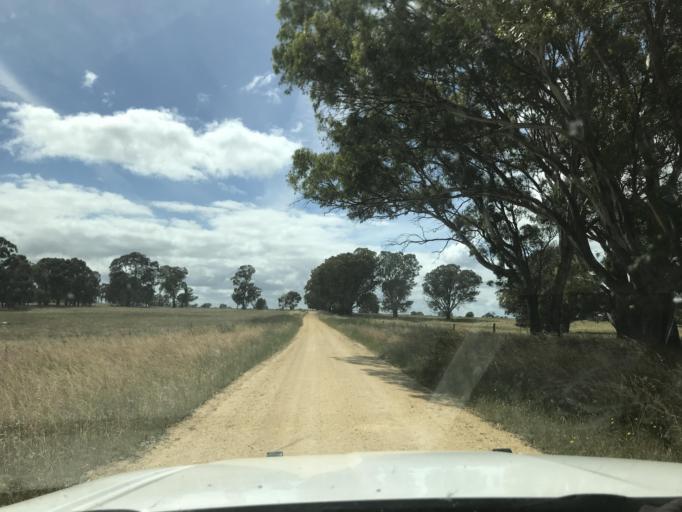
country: AU
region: South Australia
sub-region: Naracoorte and Lucindale
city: Naracoorte
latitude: -37.0200
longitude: 141.1079
